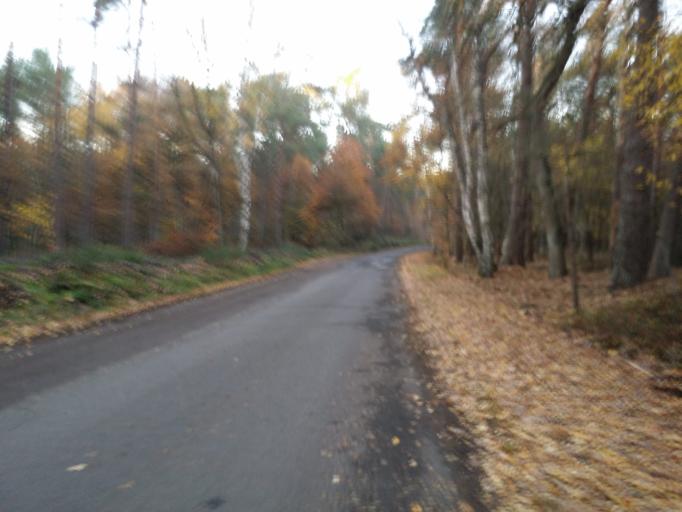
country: DE
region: Lower Saxony
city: Ahausen
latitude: 53.0764
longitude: 9.3063
